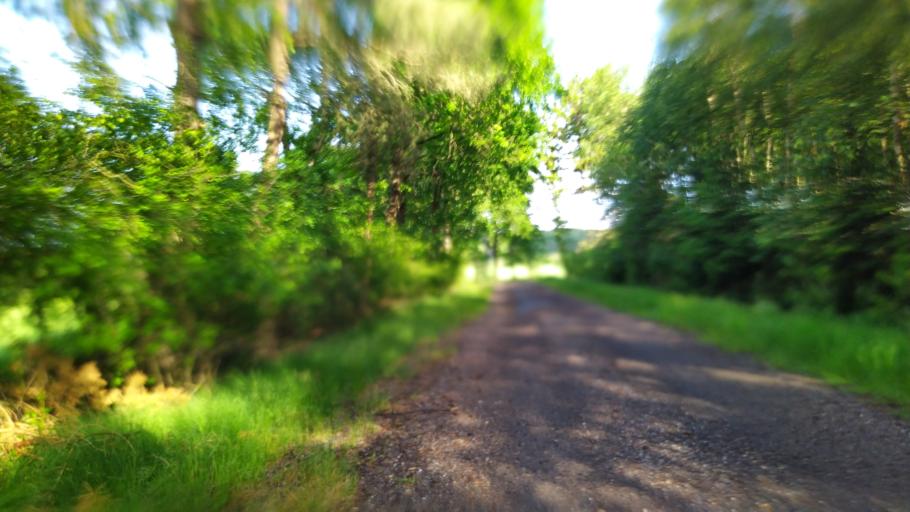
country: DE
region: Lower Saxony
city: Deinstedt
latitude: 53.4424
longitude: 9.2499
